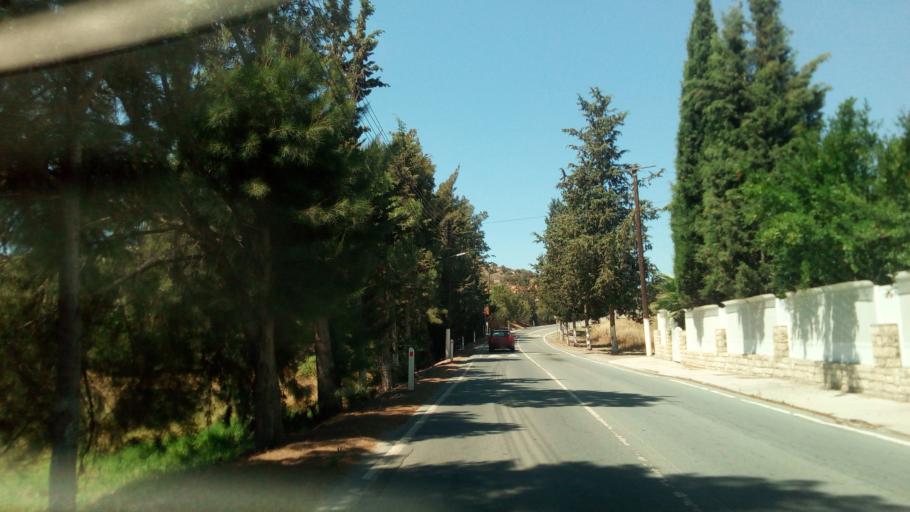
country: CY
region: Limassol
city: Pyrgos
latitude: 34.7339
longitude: 33.1755
